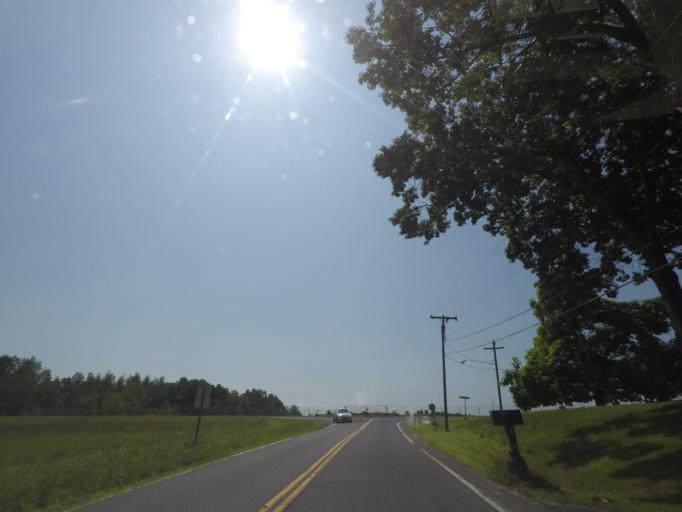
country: US
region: New York
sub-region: Saratoga County
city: Mechanicville
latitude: 42.8529
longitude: -73.7178
